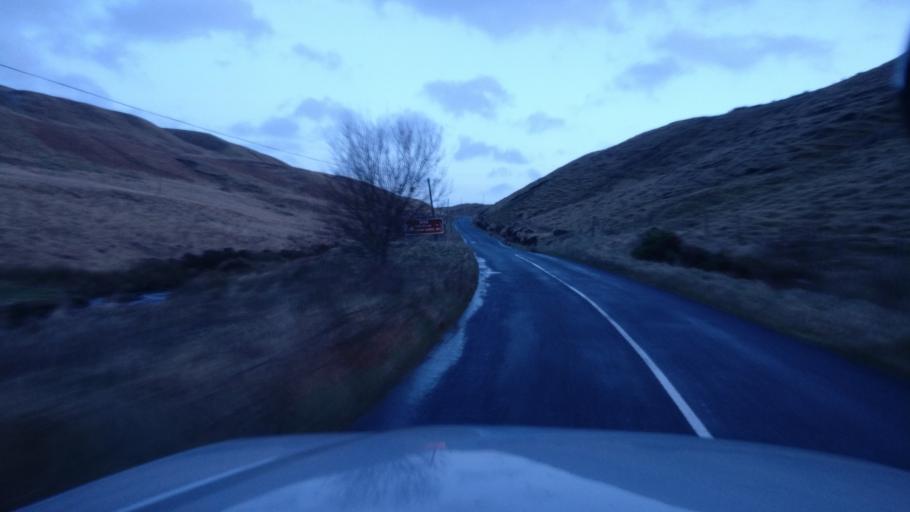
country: IE
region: Connaught
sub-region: Maigh Eo
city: Westport
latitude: 53.5900
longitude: -9.6885
